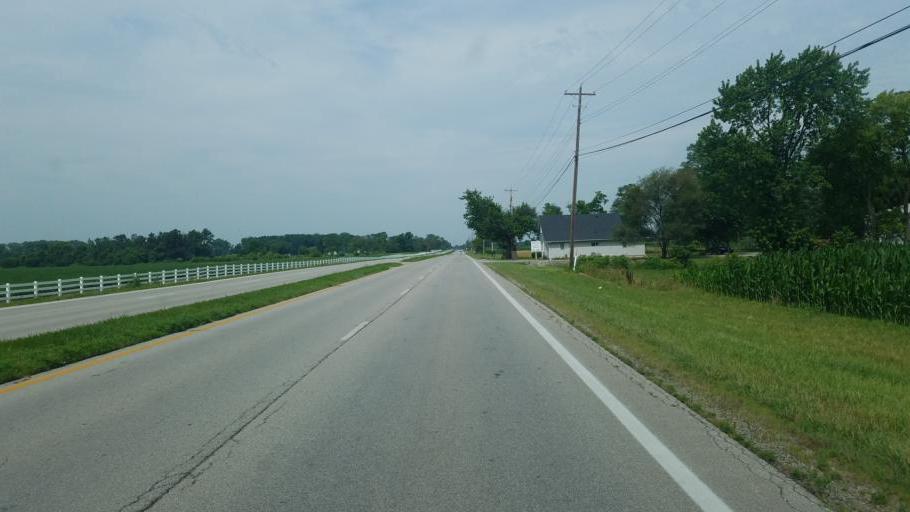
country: US
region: Ohio
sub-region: Franklin County
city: Lake Darby
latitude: 39.9489
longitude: -83.2075
